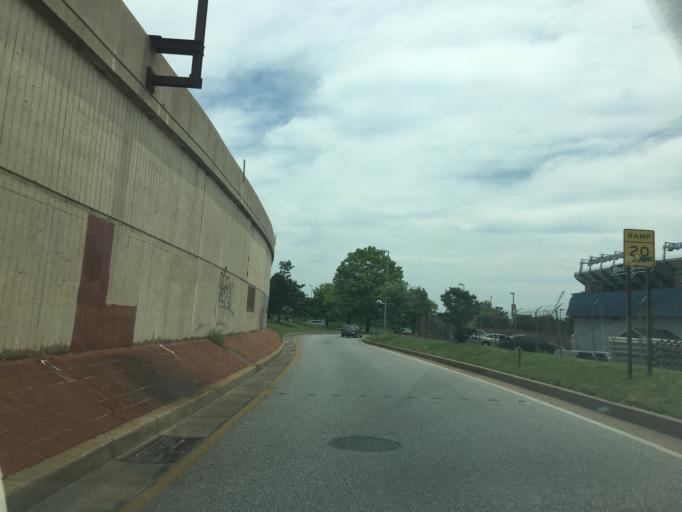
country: US
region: Maryland
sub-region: City of Baltimore
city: Baltimore
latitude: 39.2815
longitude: -76.6247
